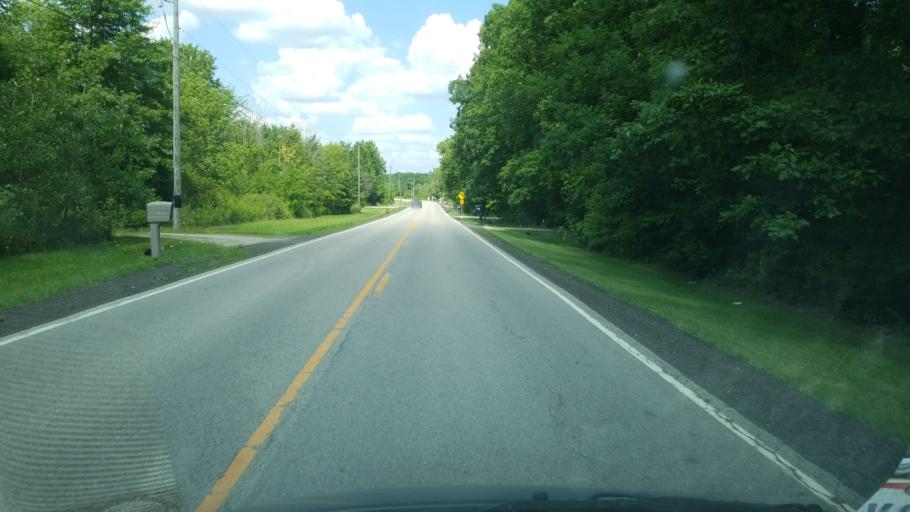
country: US
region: Ohio
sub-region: Union County
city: Marysville
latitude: 40.2805
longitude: -83.4652
